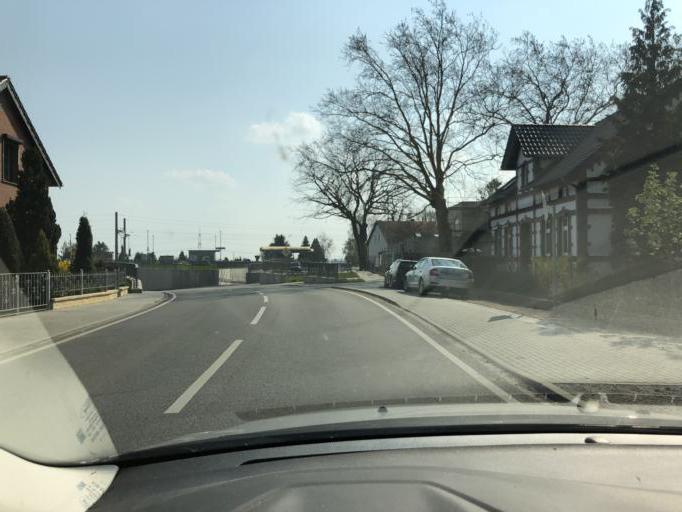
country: DE
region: Saxony-Anhalt
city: Hohenthurm
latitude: 51.5134
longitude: 12.0969
